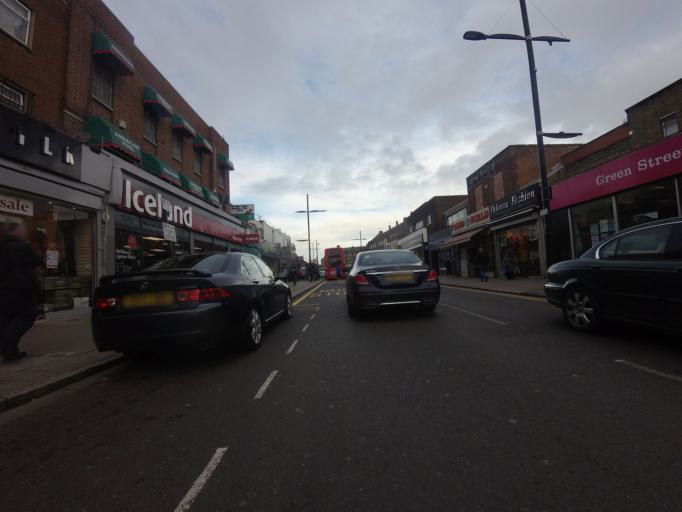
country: GB
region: England
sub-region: Greater London
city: East Ham
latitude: 51.5363
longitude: 0.0350
